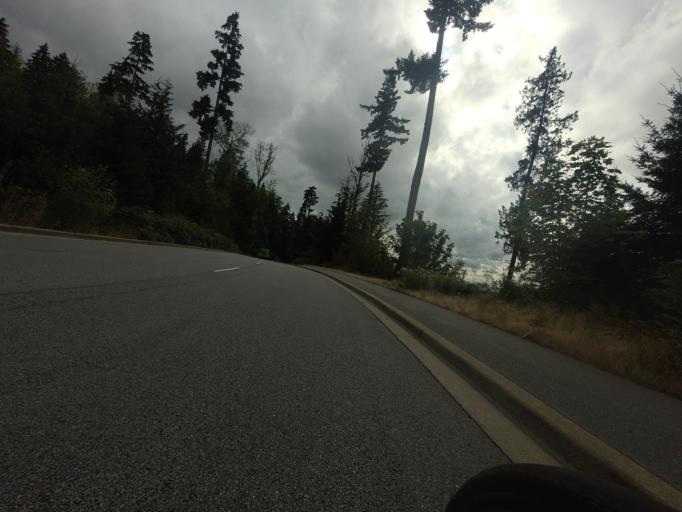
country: CA
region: British Columbia
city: West End
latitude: 49.3093
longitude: -123.1510
